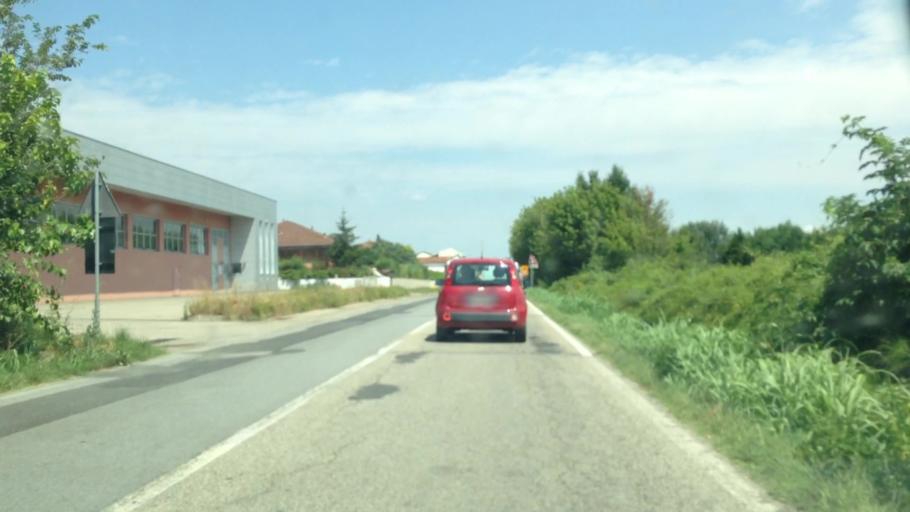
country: IT
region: Piedmont
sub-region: Provincia di Asti
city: Portacomaro
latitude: 44.9404
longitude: 8.2245
